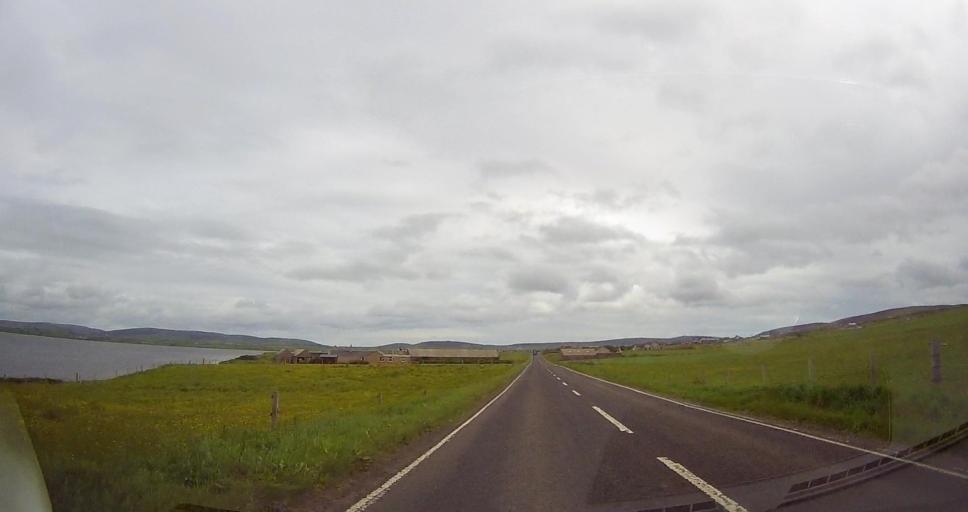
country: GB
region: Scotland
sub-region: Orkney Islands
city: Stromness
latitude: 58.9851
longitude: -3.2385
